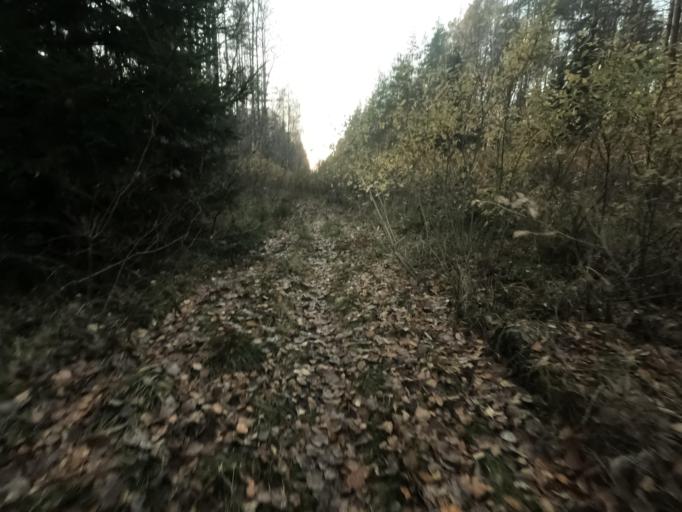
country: RU
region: St.-Petersburg
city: Komarovo
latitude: 60.2011
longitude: 29.8123
